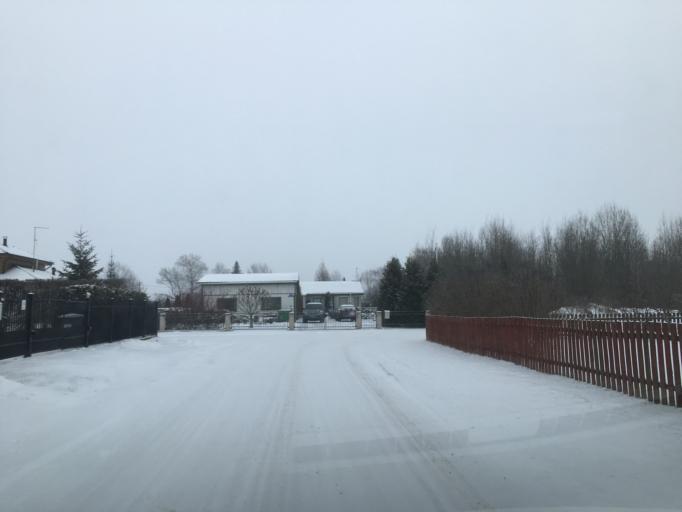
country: EE
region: Tartu
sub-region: Tartu linn
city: Tartu
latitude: 58.3510
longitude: 26.6708
